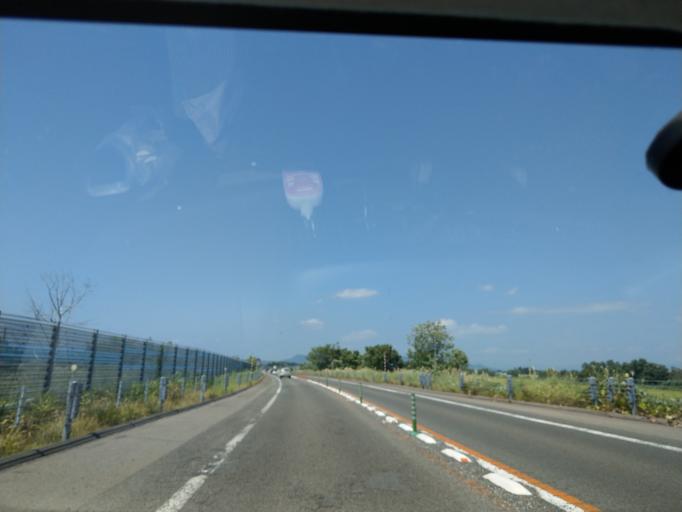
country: JP
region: Akita
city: Yokotemachi
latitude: 39.3542
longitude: 140.4953
